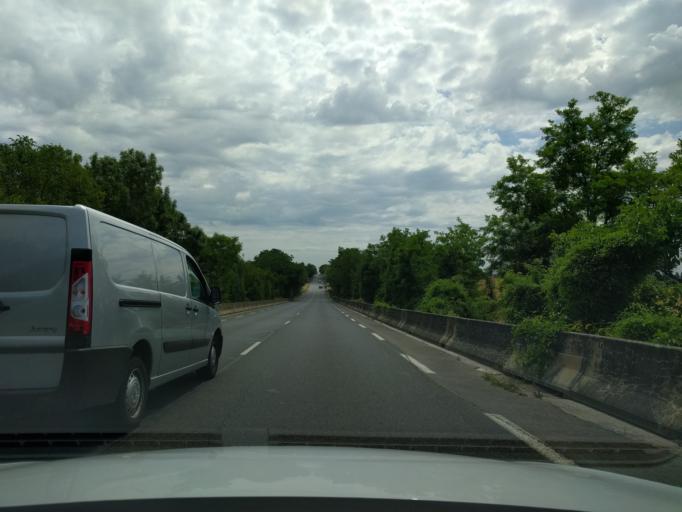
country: FR
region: Poitou-Charentes
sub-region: Departement des Deux-Sevres
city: Bessines
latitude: 46.3445
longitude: -0.4997
